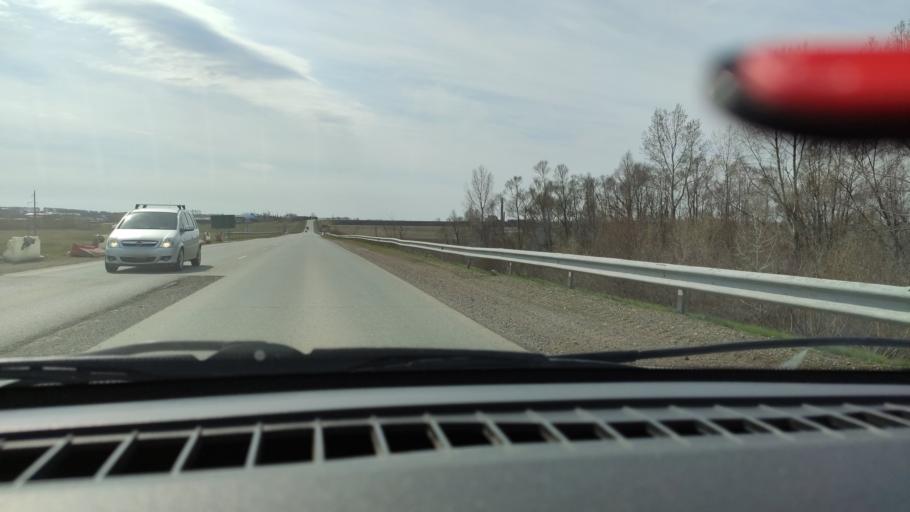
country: RU
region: Bashkortostan
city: Dyurtyuli
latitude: 55.5094
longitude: 54.8350
